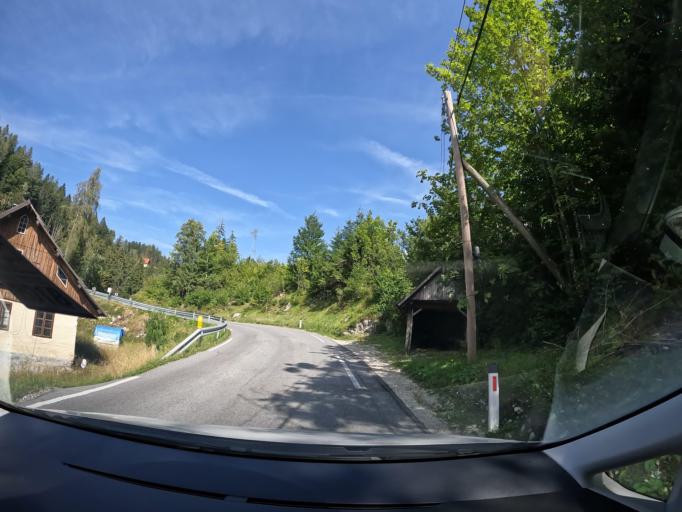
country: AT
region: Carinthia
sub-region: Politischer Bezirk Villach Land
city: Velden am Woerthersee
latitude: 46.5918
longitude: 14.0659
